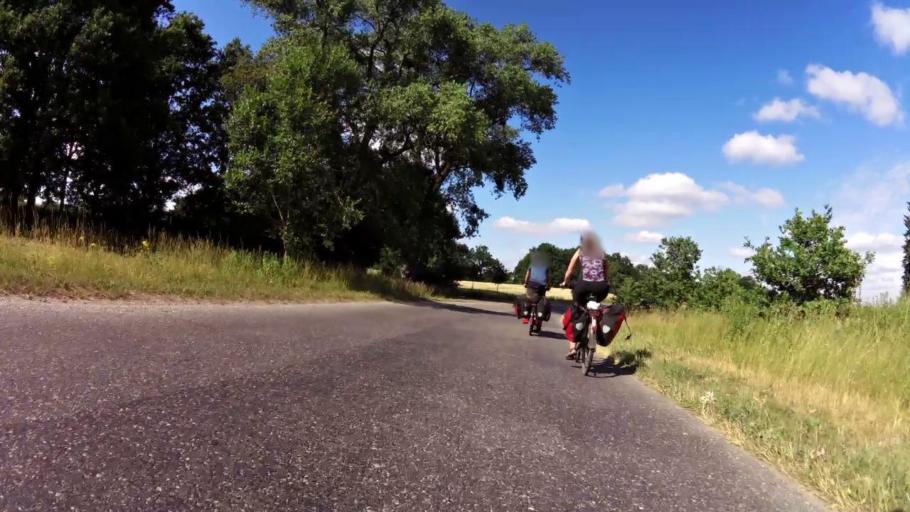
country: PL
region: West Pomeranian Voivodeship
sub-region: Powiat lobeski
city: Lobez
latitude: 53.6522
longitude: 15.6764
